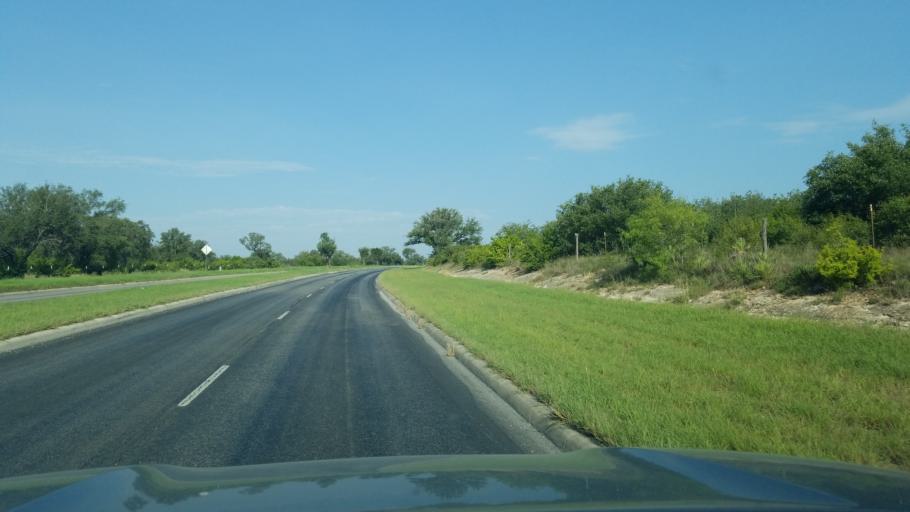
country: US
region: Texas
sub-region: Bexar County
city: Leon Valley
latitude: 29.4598
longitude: -98.7400
